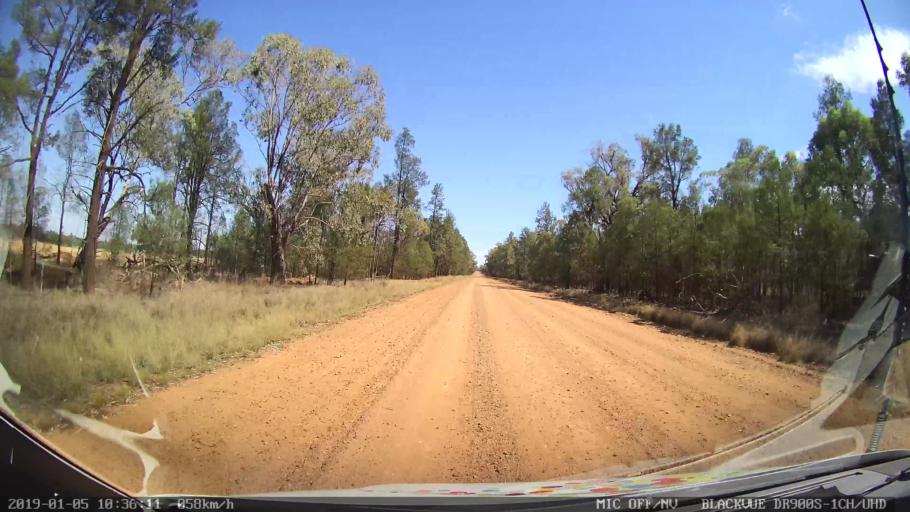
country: AU
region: New South Wales
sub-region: Gilgandra
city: Gilgandra
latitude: -31.4841
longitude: 148.9260
